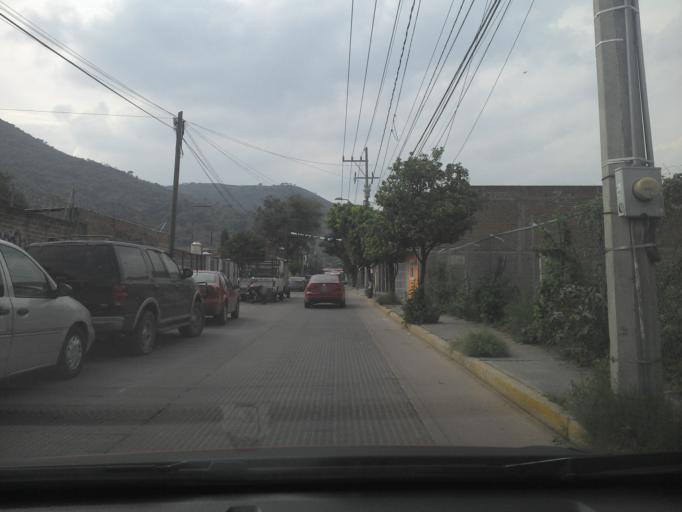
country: MX
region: Jalisco
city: Tlajomulco de Zuniga
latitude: 20.4775
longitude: -103.4507
